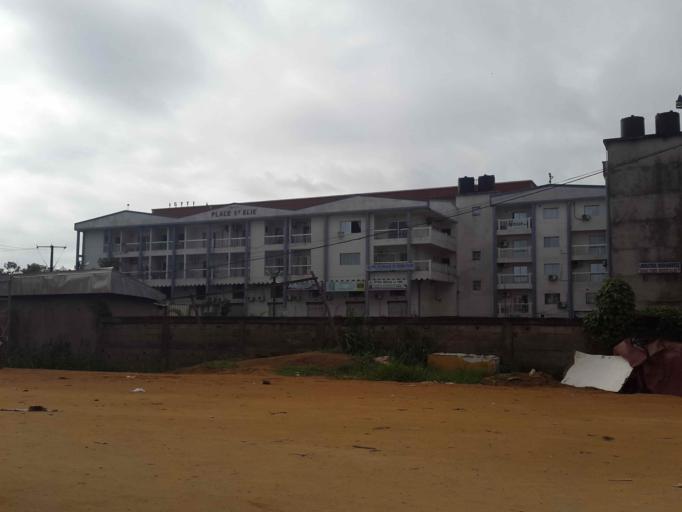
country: CM
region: Littoral
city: Douala
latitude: 4.0848
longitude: 9.7335
